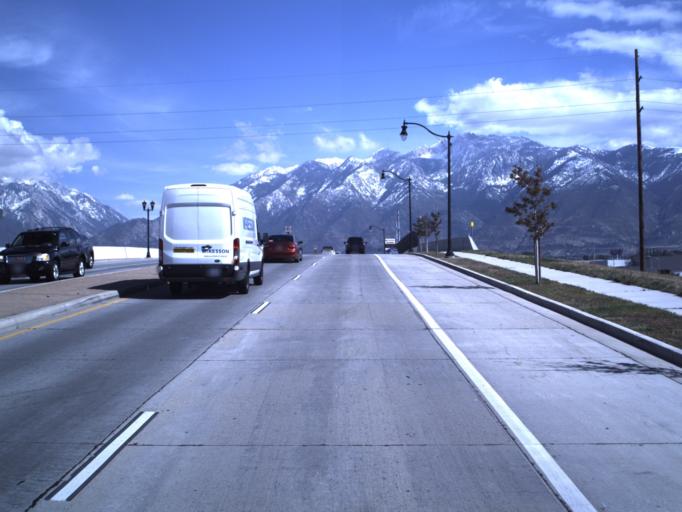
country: US
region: Utah
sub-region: Salt Lake County
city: South Jordan
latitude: 40.5443
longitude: -111.9043
